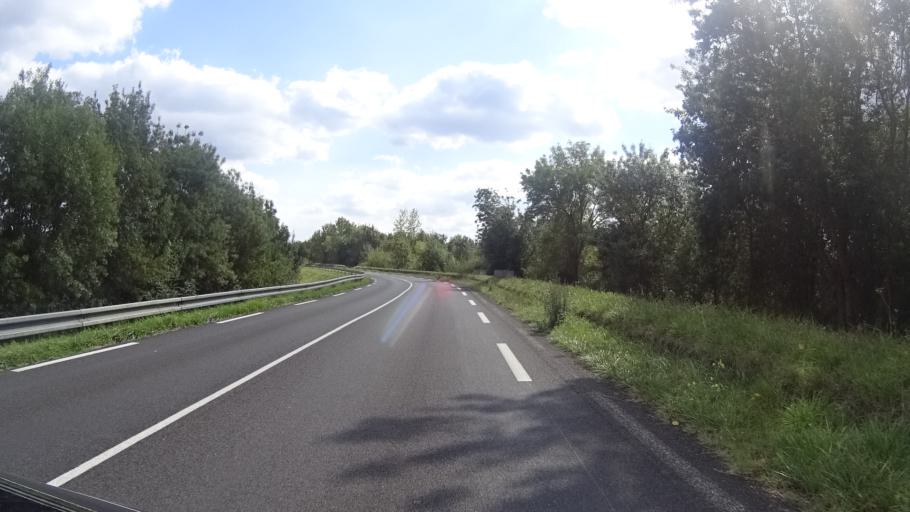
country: FR
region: Pays de la Loire
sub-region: Departement de Maine-et-Loire
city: Gennes
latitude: 47.3665
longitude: -0.2523
